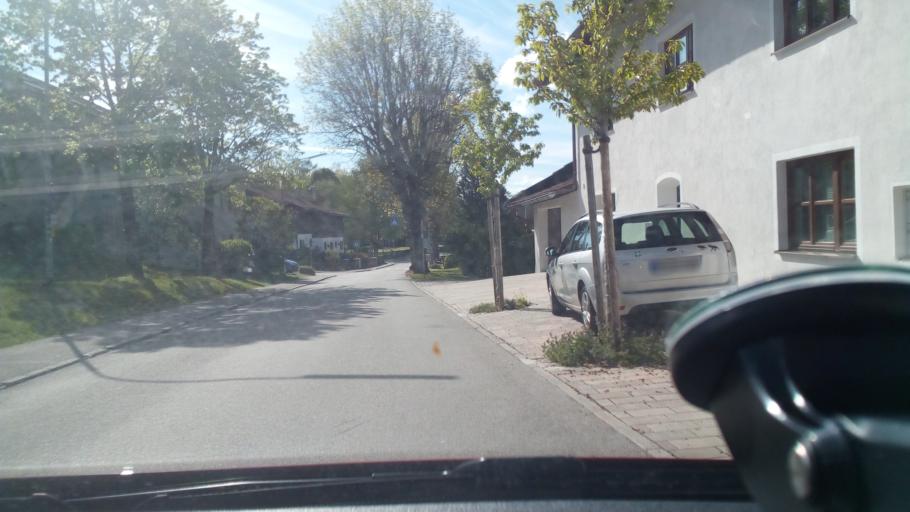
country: DE
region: Bavaria
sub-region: Upper Bavaria
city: Holzkirchen
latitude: 47.8777
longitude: 11.6971
